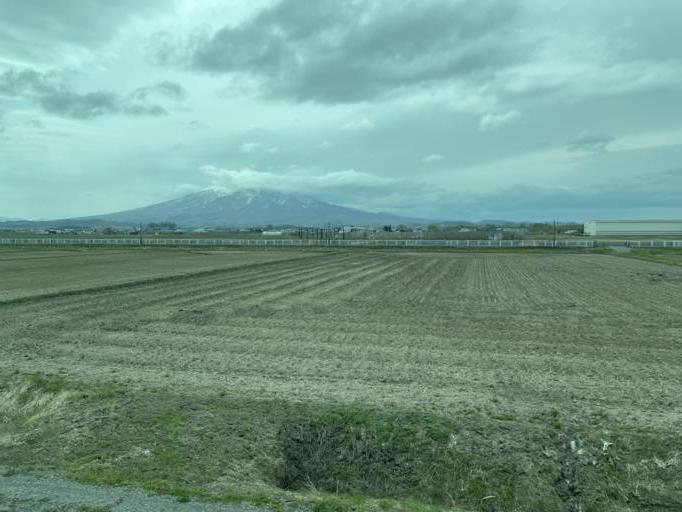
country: JP
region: Aomori
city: Goshogawara
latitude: 40.7439
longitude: 140.4346
